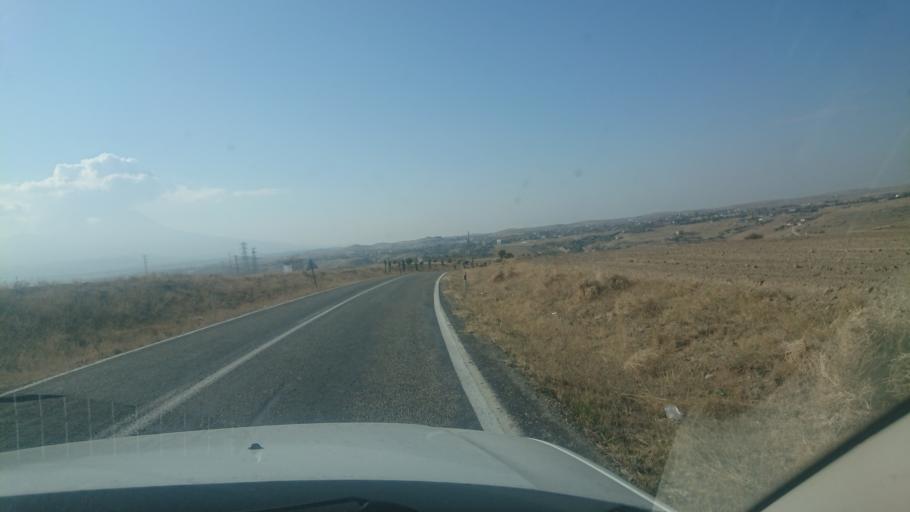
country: TR
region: Aksaray
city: Guzelyurt
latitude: 38.2451
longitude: 34.3220
